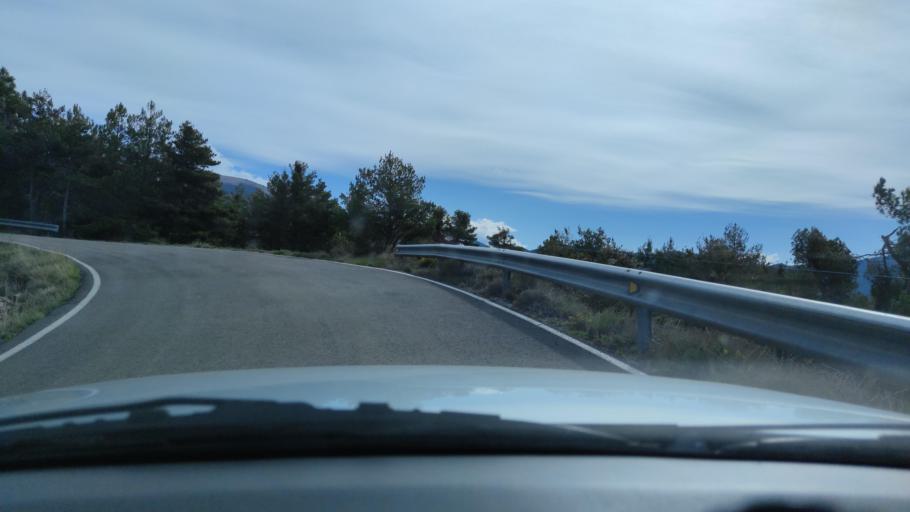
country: ES
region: Catalonia
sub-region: Provincia de Lleida
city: Alas i Cerc
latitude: 42.2505
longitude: 1.4892
